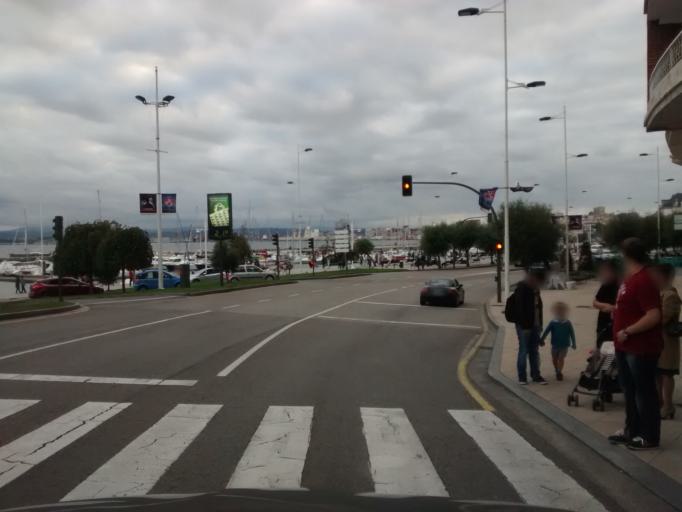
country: ES
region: Cantabria
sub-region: Provincia de Cantabria
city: Santander
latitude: 43.4630
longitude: -3.7915
